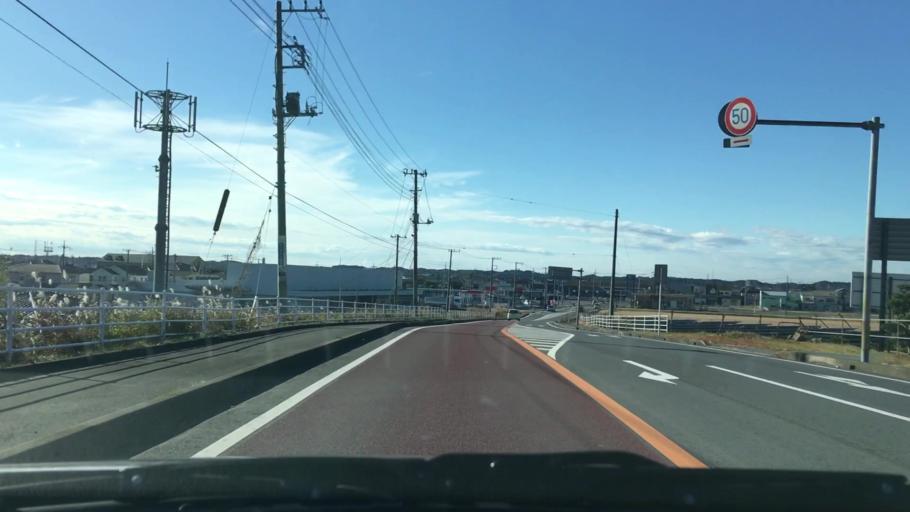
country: JP
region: Chiba
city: Omigawa
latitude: 35.8630
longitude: 140.6120
